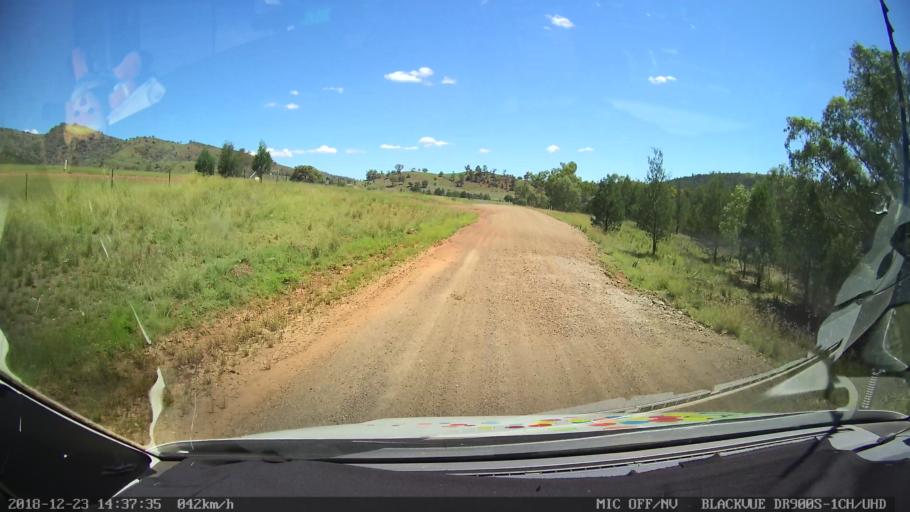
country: AU
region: New South Wales
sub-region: Tamworth Municipality
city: Manilla
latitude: -30.6164
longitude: 150.9070
